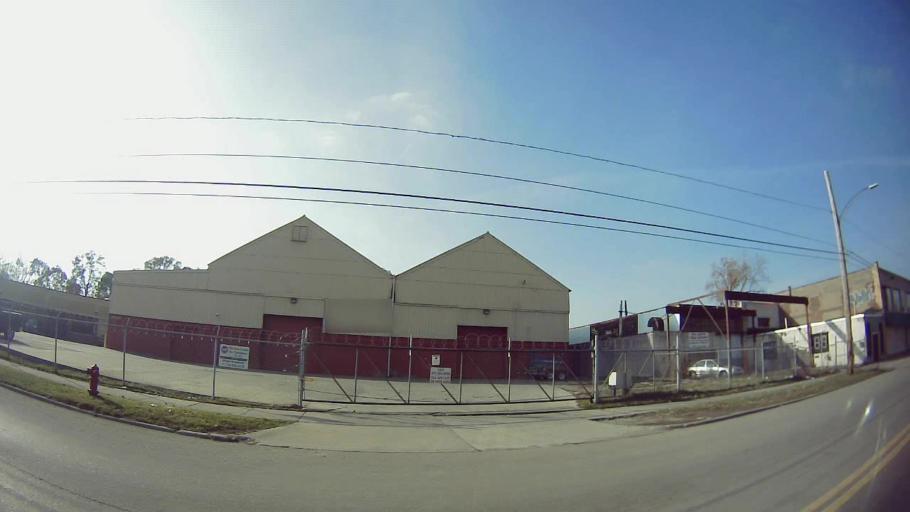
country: US
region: Michigan
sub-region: Oakland County
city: Hazel Park
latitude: 42.4357
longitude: -83.1024
